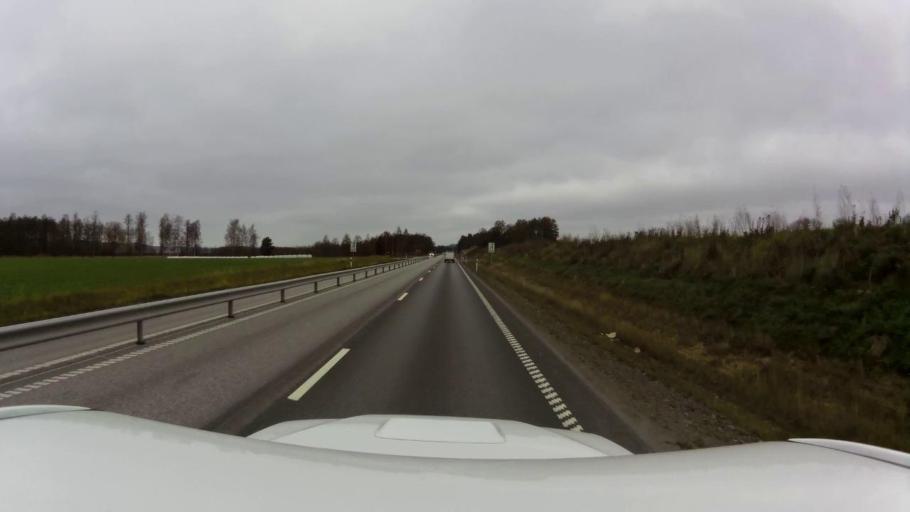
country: SE
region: OEstergoetland
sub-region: Kinda Kommun
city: Rimforsa
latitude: 58.1463
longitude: 15.6808
